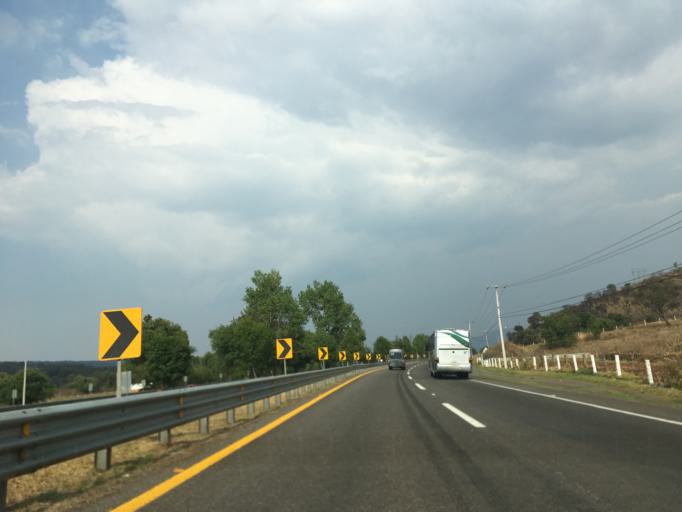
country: MX
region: Michoacan
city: Lagunillas
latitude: 19.5602
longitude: -101.4050
